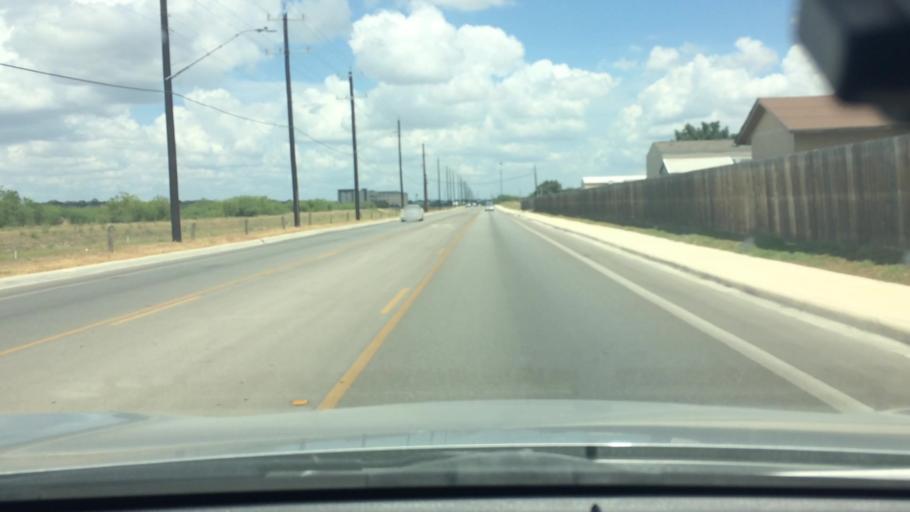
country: US
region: Texas
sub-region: Bexar County
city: China Grove
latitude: 29.3410
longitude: -98.4242
